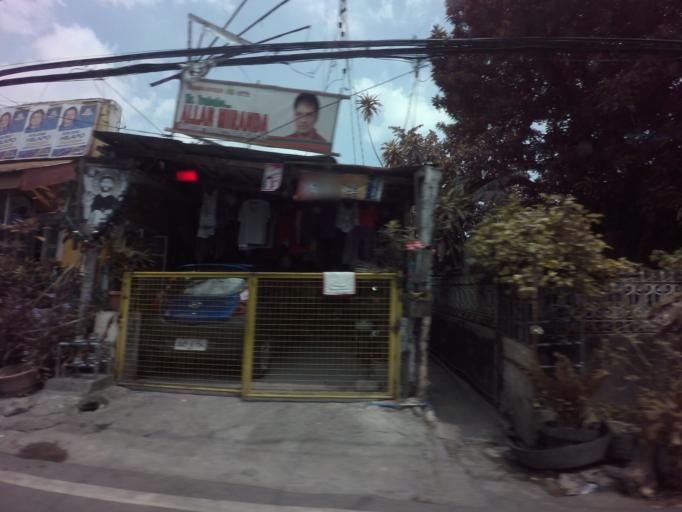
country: PH
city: Sambayanihan People's Village
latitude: 14.4557
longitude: 121.0527
